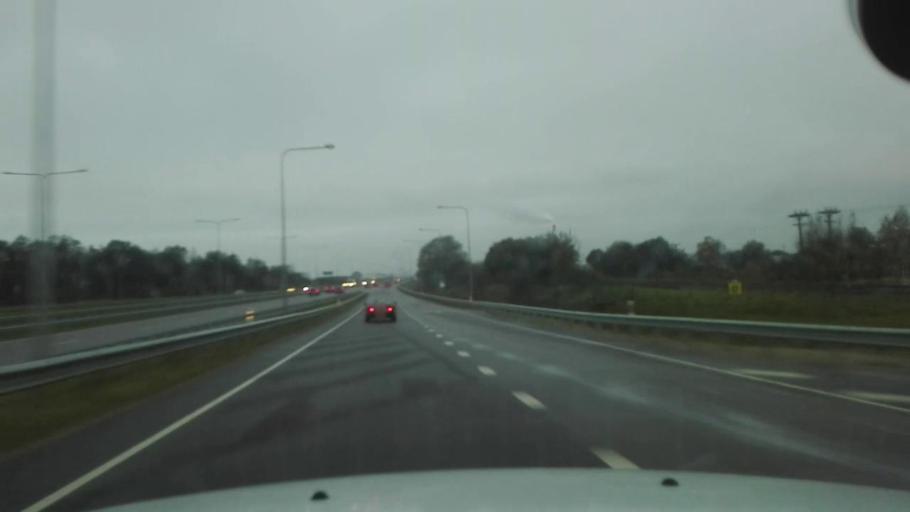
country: EE
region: Harju
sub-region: Joelaehtme vald
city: Loo
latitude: 59.4567
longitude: 24.9831
